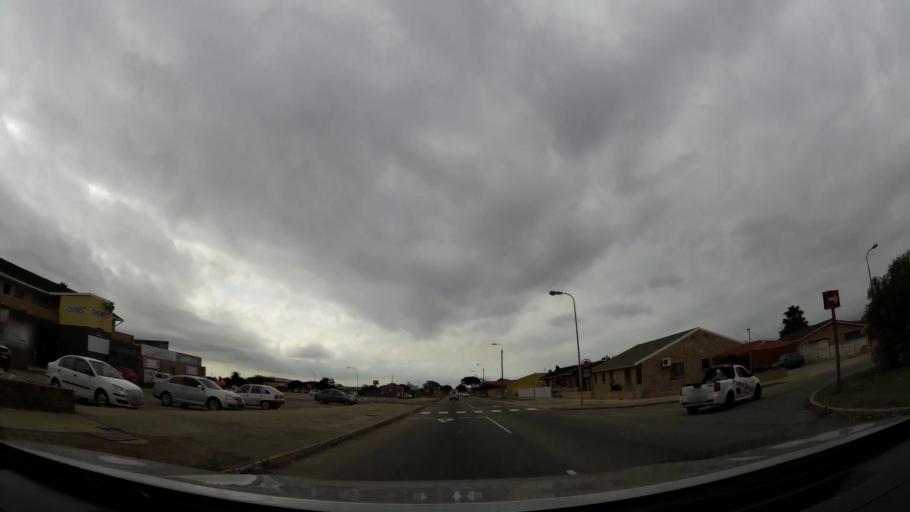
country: ZA
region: Eastern Cape
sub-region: Nelson Mandela Bay Metropolitan Municipality
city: Port Elizabeth
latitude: -33.9024
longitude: 25.5622
